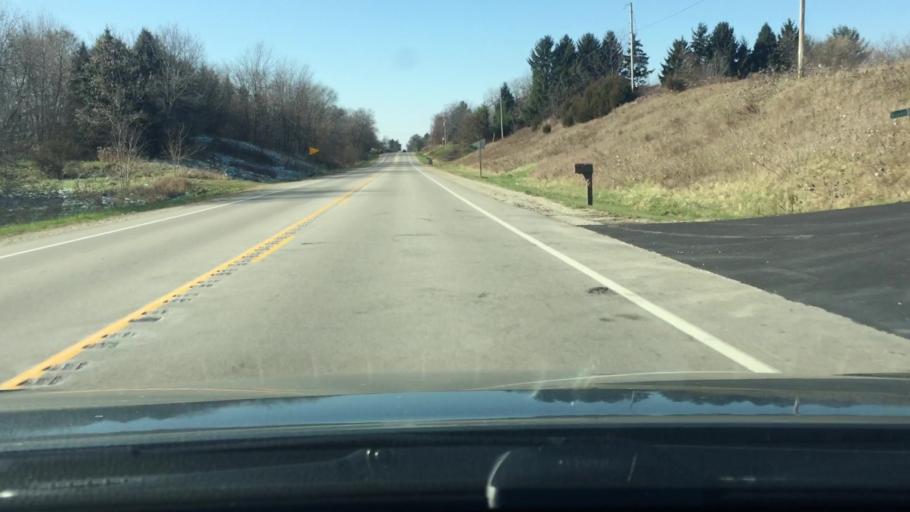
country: US
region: Wisconsin
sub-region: Jefferson County
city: Lake Ripley
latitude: 43.0118
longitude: -88.9714
